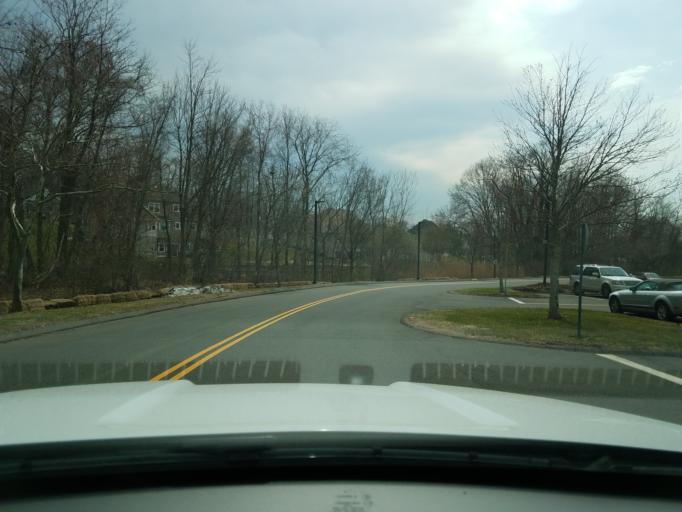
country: US
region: Connecticut
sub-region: Hartford County
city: Newington
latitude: 41.6718
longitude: -72.7130
